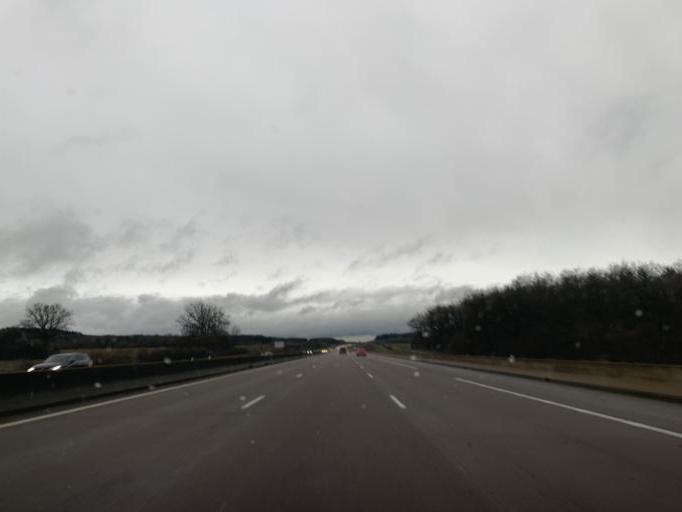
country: FR
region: Champagne-Ardenne
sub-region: Departement de la Haute-Marne
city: Langres
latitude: 47.8528
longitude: 5.2290
